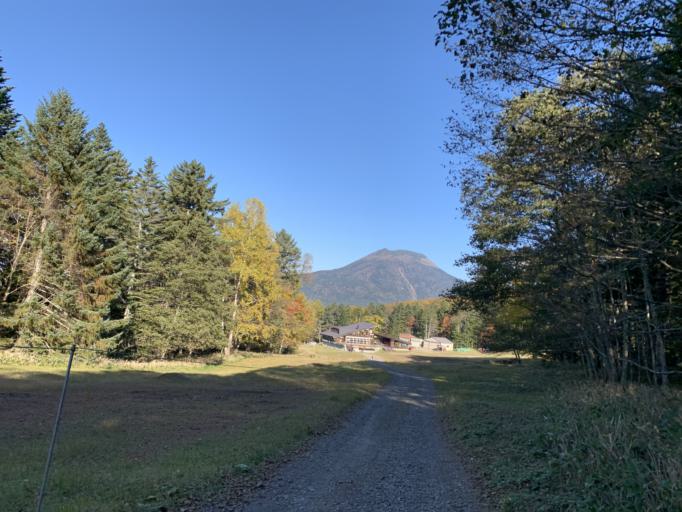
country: JP
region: Hokkaido
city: Bihoro
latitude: 43.4224
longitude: 144.0824
